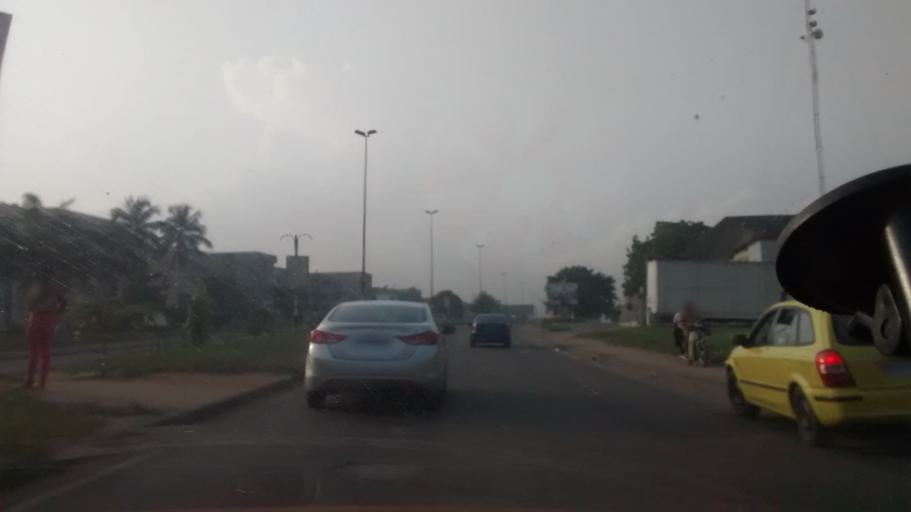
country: CI
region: Lagunes
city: Abobo
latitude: 5.3719
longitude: -3.9984
